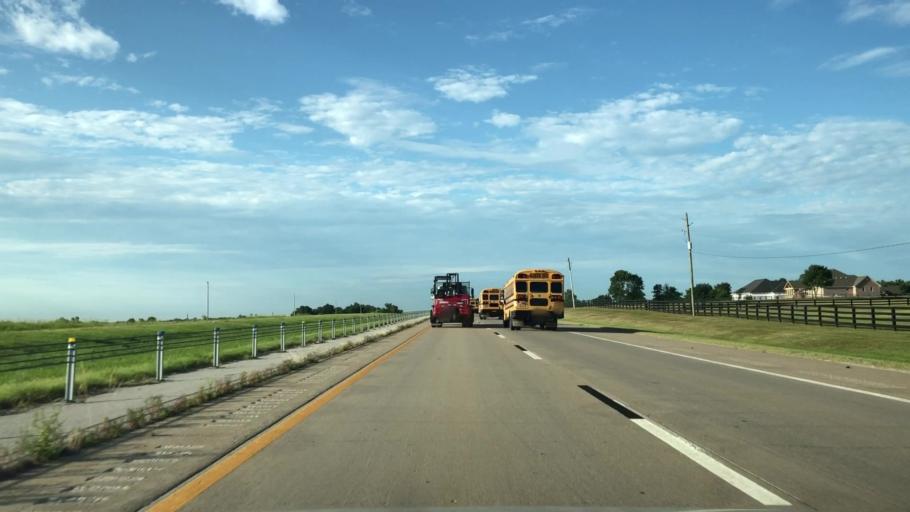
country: US
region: Oklahoma
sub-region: Osage County
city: Skiatook
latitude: 36.4666
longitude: -95.9207
